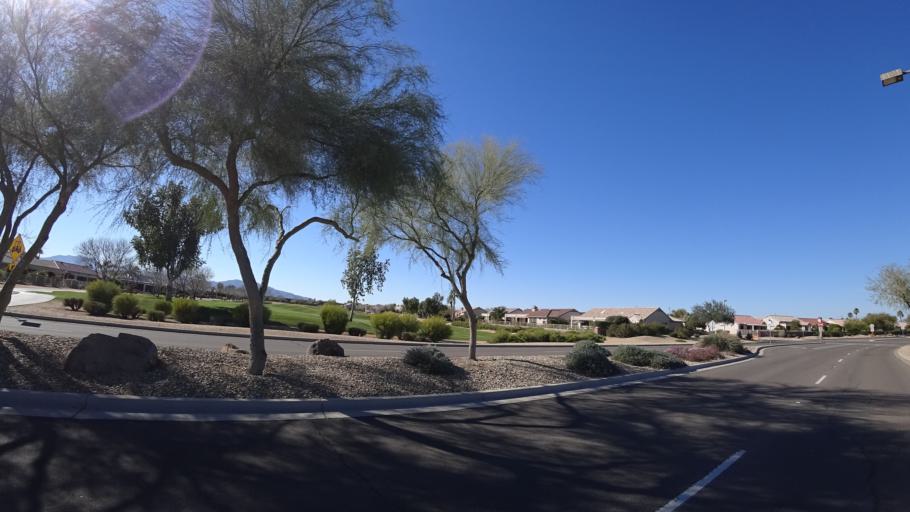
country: US
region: Arizona
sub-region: Maricopa County
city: Sun City West
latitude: 33.6521
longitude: -112.4131
